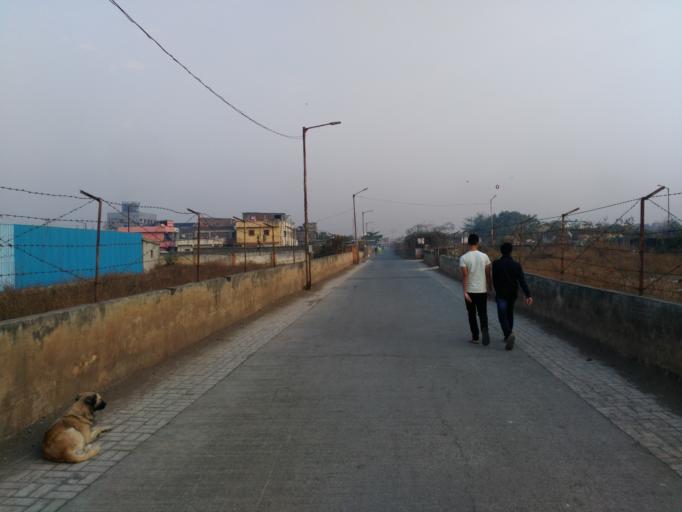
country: IN
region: Maharashtra
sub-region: Pune Division
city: Pune
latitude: 18.4583
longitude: 73.8730
